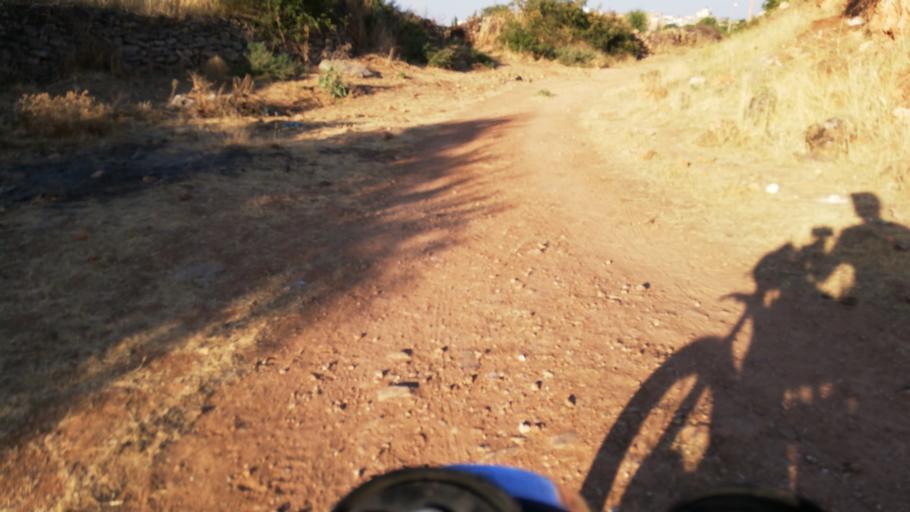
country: TR
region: Mardin
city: Kindirip
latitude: 37.4457
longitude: 41.2121
